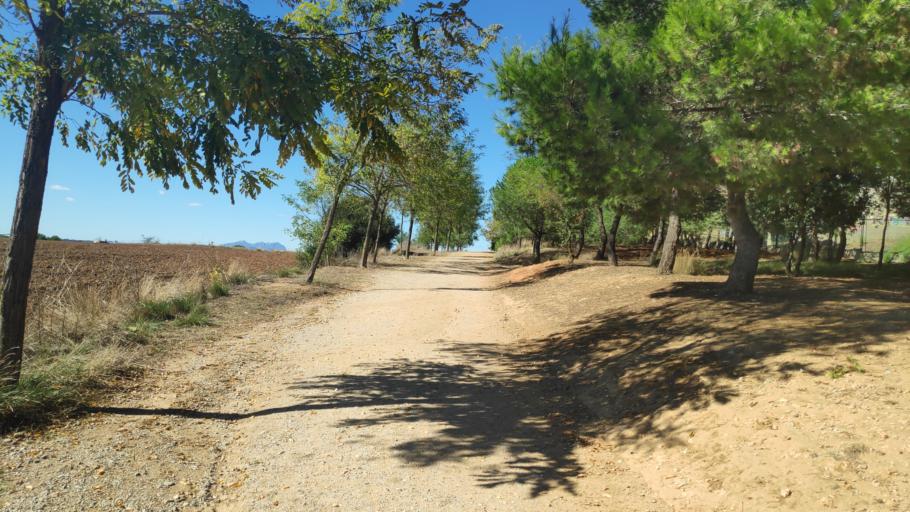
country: ES
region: Catalonia
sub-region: Provincia de Barcelona
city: Mollet del Valles
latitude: 41.5451
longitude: 2.1980
